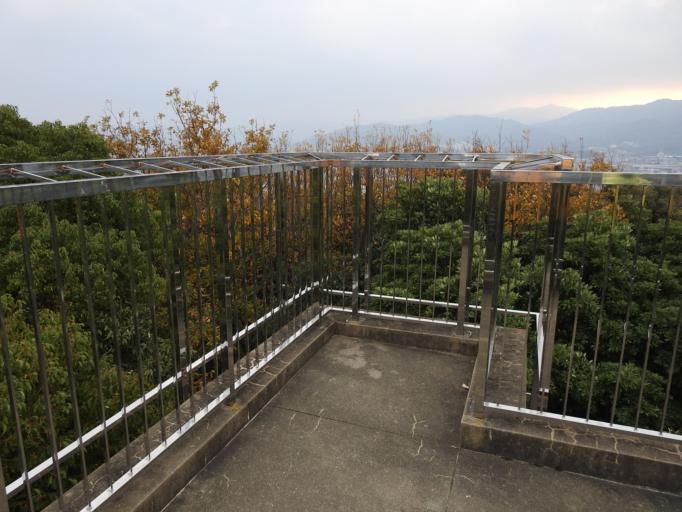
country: JP
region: Fukuoka
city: Fukuoka-shi
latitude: 33.5592
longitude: 130.3935
